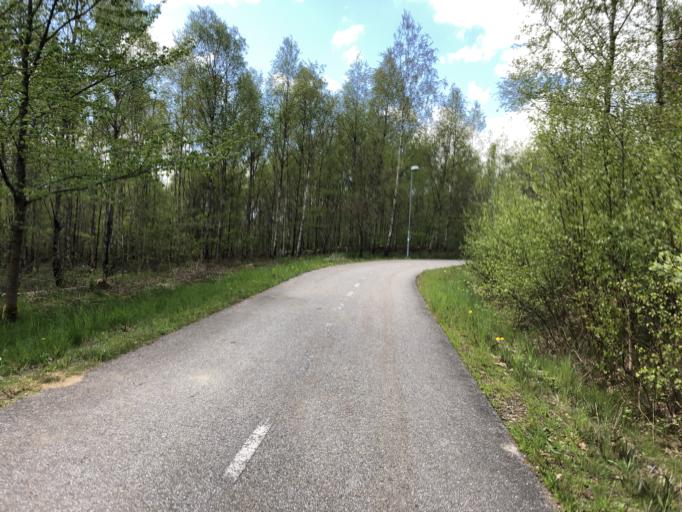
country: SE
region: Skane
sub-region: Lunds Kommun
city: Genarp
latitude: 55.6920
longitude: 13.3494
